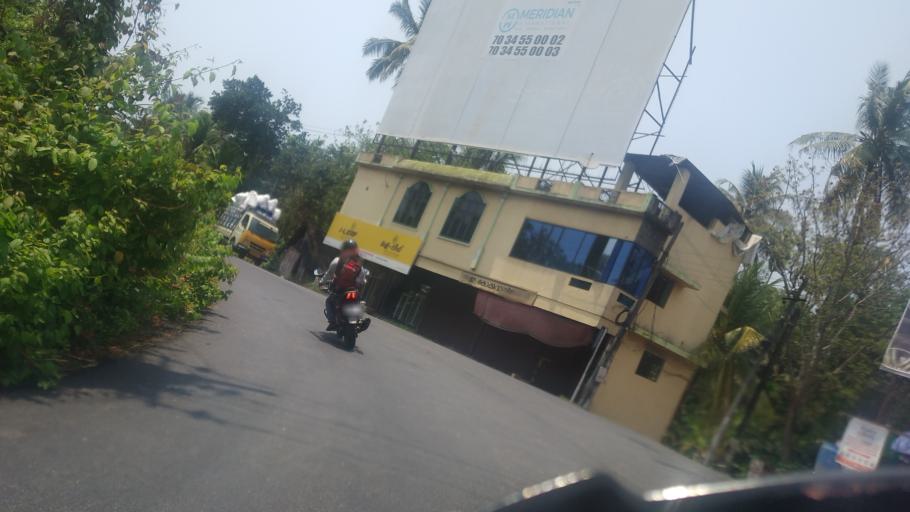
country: IN
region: Kerala
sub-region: Thrissur District
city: Kodungallur
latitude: 10.2483
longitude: 76.1884
